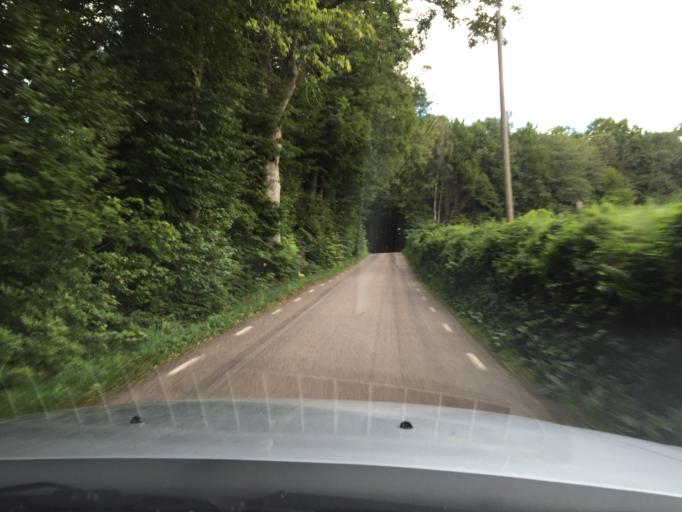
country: SE
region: Skane
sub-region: Hassleholms Kommun
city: Vinslov
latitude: 55.9685
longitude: 13.8639
